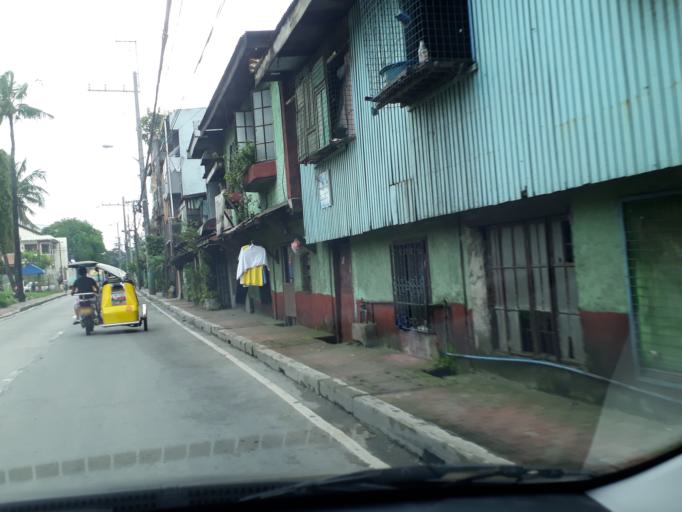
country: PH
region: Calabarzon
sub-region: Province of Rizal
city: Valenzuela
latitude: 14.7099
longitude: 120.9624
